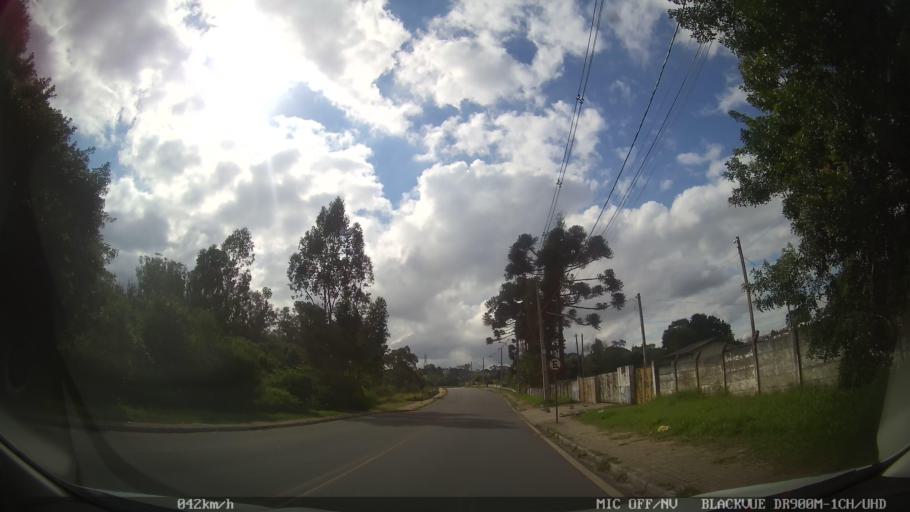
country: BR
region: Parana
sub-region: Pinhais
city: Pinhais
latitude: -25.3827
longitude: -49.2037
